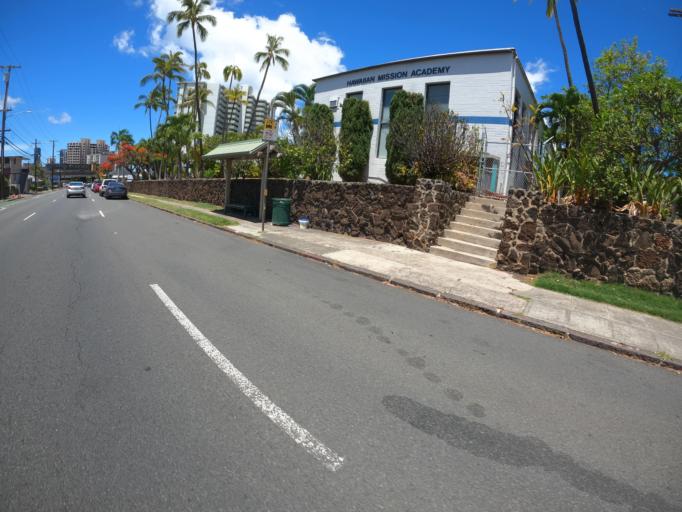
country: US
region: Hawaii
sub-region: Honolulu County
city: Honolulu
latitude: 21.3055
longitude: -157.8431
